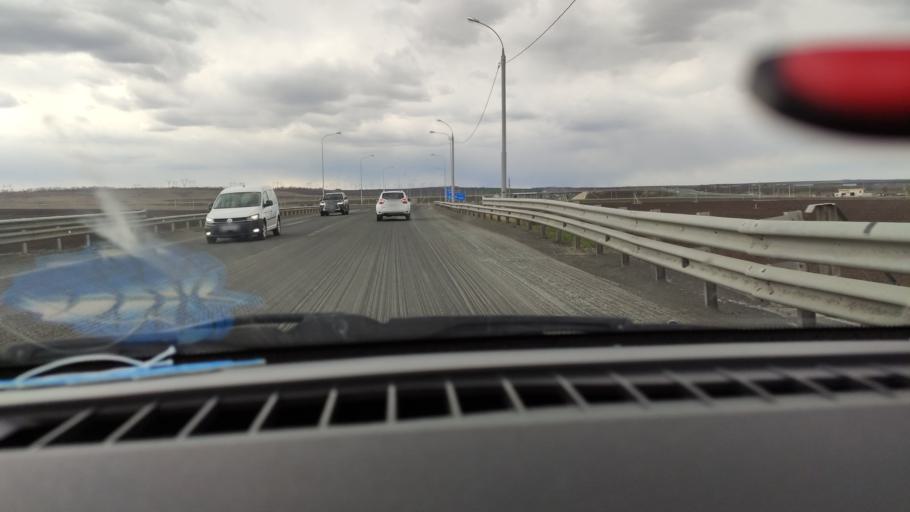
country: RU
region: Saratov
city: Yelshanka
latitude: 51.7985
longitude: 46.1804
